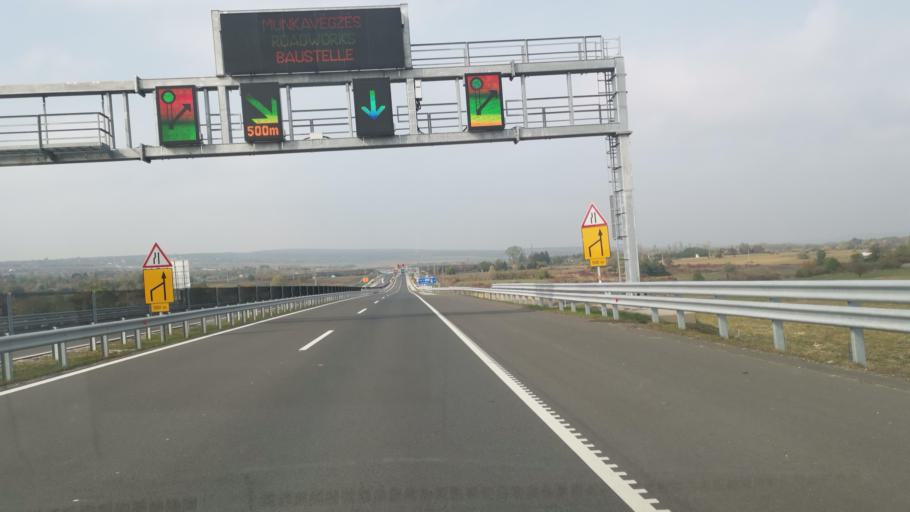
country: HU
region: Gyor-Moson-Sopron
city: Sopron
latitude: 47.7005
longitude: 16.6141
